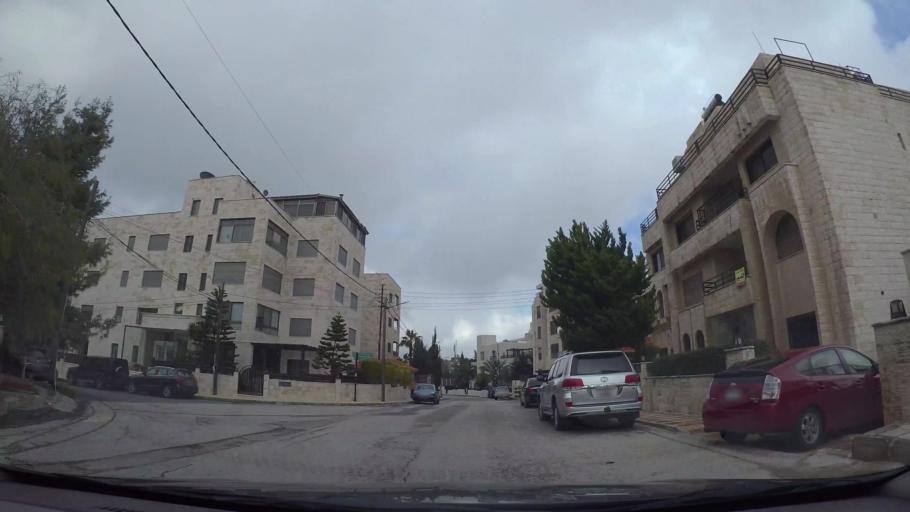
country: JO
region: Amman
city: Wadi as Sir
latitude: 31.9484
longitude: 35.8769
